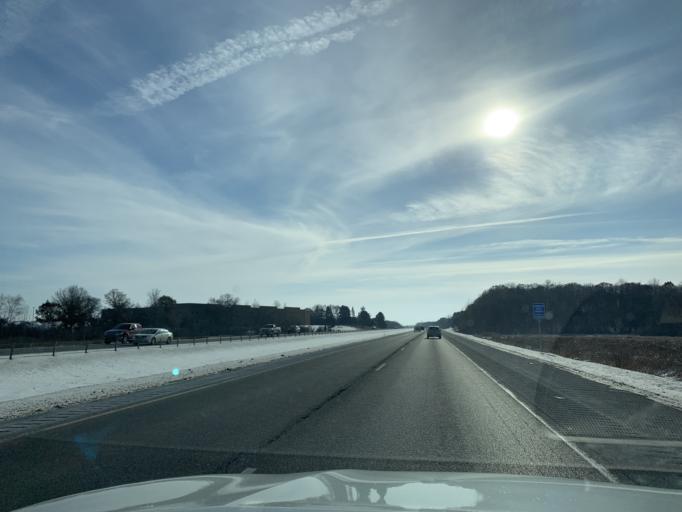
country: US
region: Minnesota
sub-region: Chisago County
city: Wyoming
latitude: 45.3199
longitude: -93.0036
